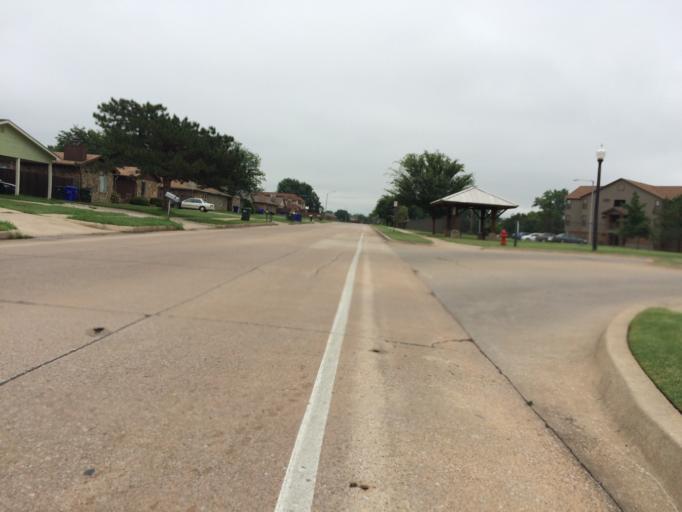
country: US
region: Oklahoma
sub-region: Cleveland County
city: Norman
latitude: 35.2090
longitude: -97.4160
